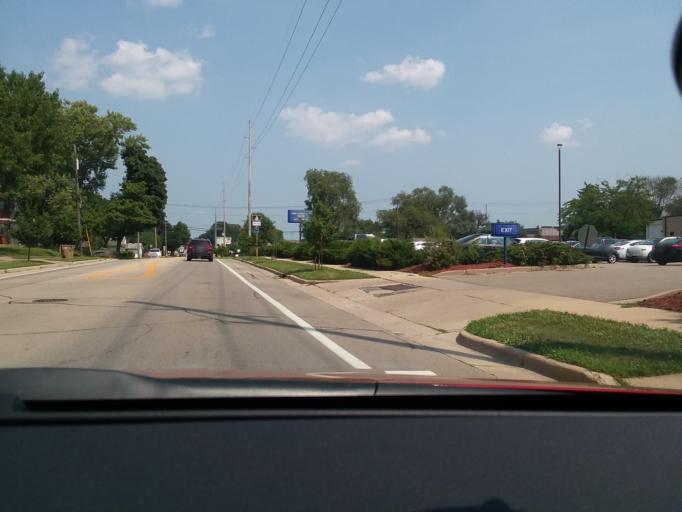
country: US
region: Wisconsin
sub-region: Dane County
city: Maple Bluff
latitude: 43.1142
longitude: -89.3616
